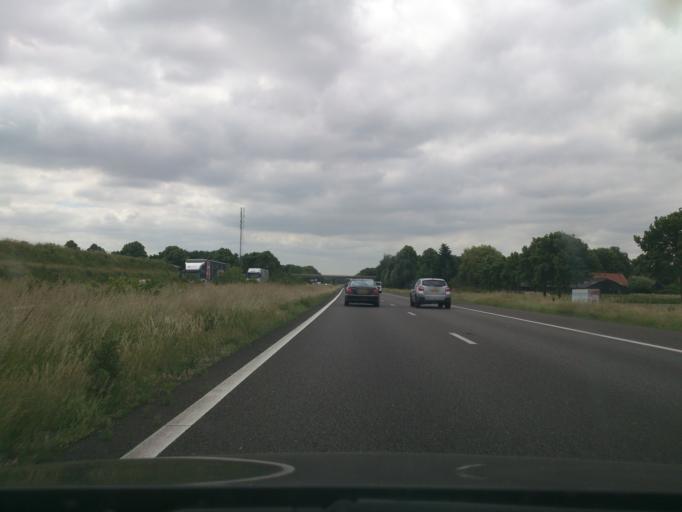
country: NL
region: North Brabant
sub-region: Gemeente Landerd
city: Schaijk
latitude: 51.7737
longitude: 5.6324
